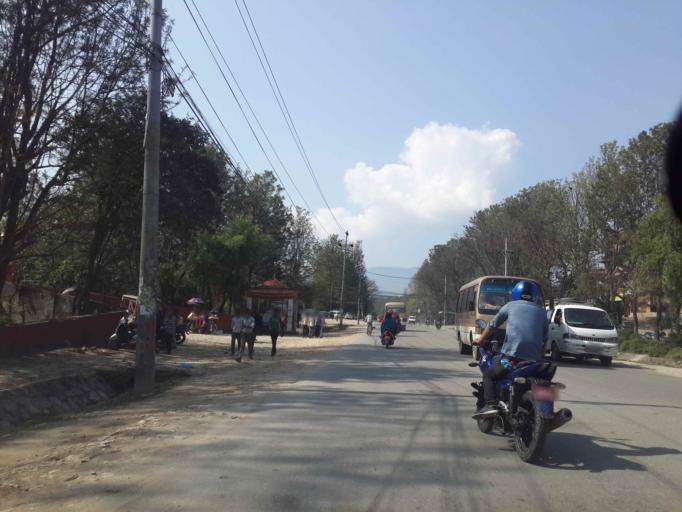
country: NP
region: Central Region
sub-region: Bagmati Zone
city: Kathmandu
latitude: 27.7336
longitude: 85.3431
